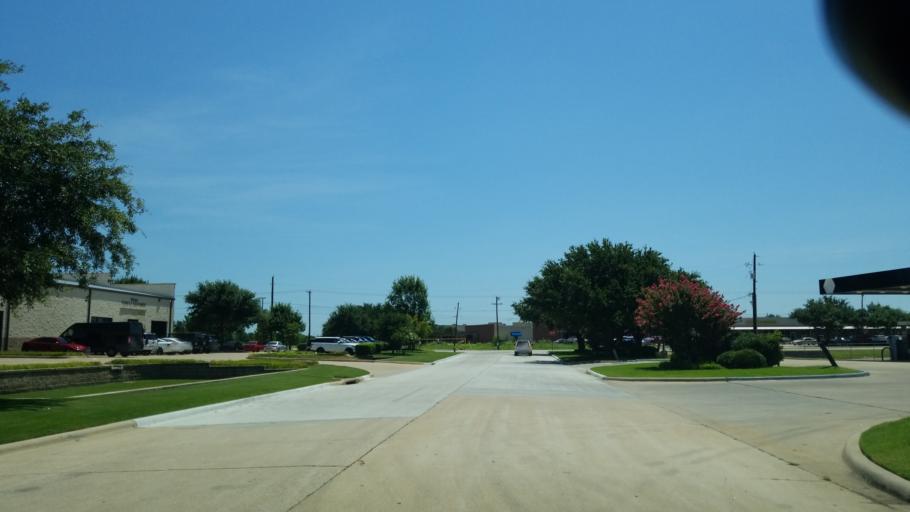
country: US
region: Texas
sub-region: Dallas County
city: Farmers Branch
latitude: 32.9386
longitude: -96.9264
